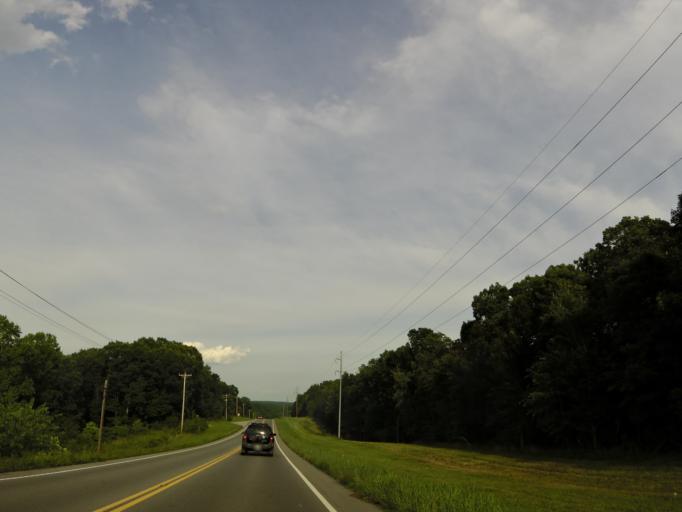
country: US
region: Tennessee
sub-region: Humphreys County
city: McEwen
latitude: 36.1037
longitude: -87.6194
